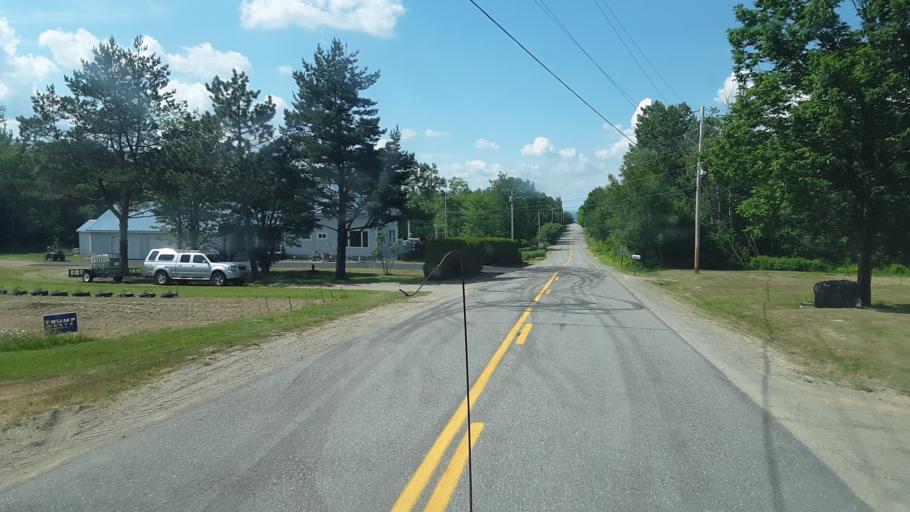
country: US
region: Maine
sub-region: Washington County
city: Calais
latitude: 45.0872
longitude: -67.5029
